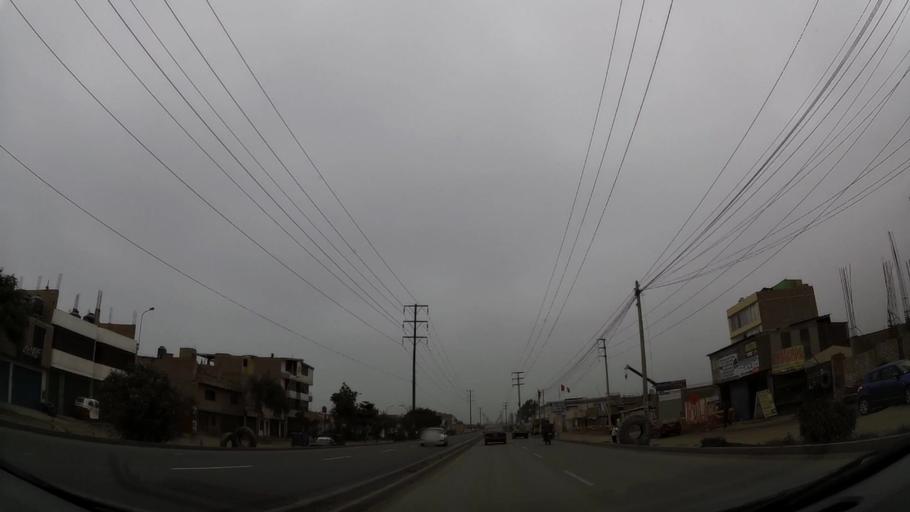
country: PE
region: Lima
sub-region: Lima
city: Punta Hermosa
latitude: -12.2921
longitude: -76.8552
